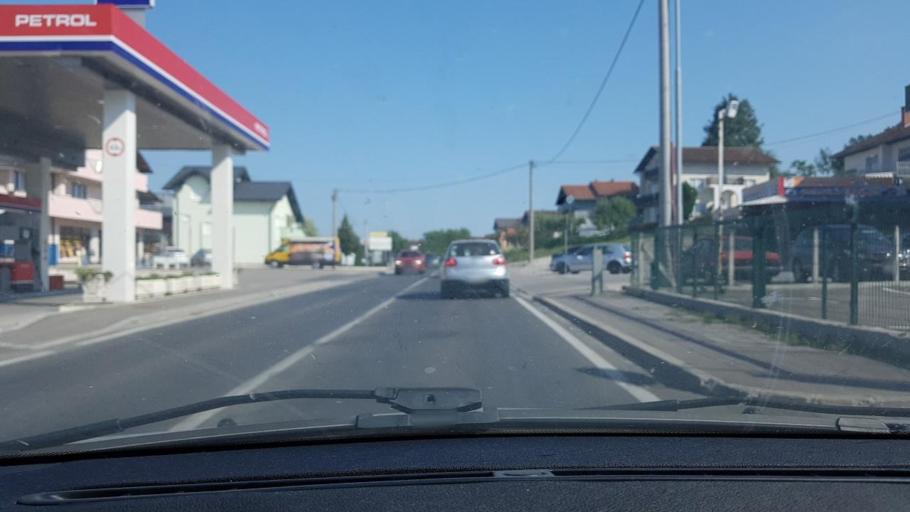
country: BA
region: Federation of Bosnia and Herzegovina
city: Cazin
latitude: 44.9695
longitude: 15.8989
